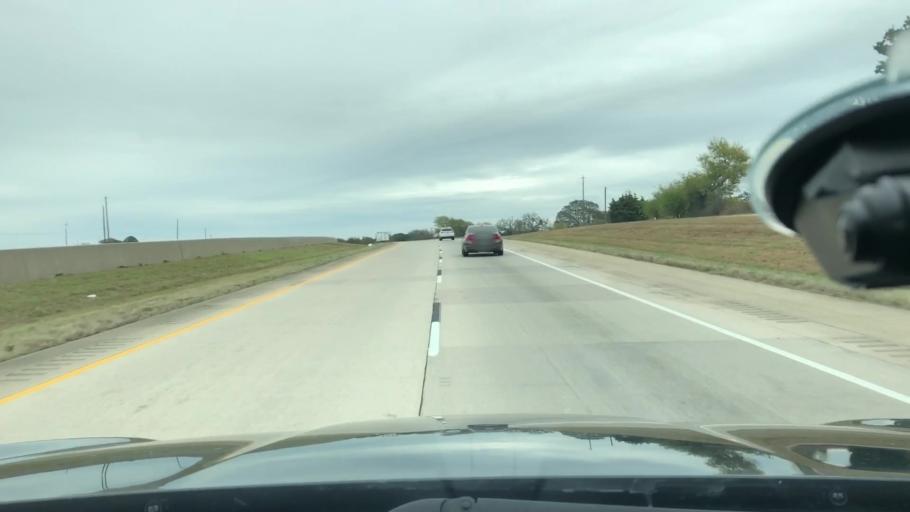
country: US
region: Texas
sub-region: Hopkins County
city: Sulphur Springs
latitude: 33.1204
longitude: -95.7259
